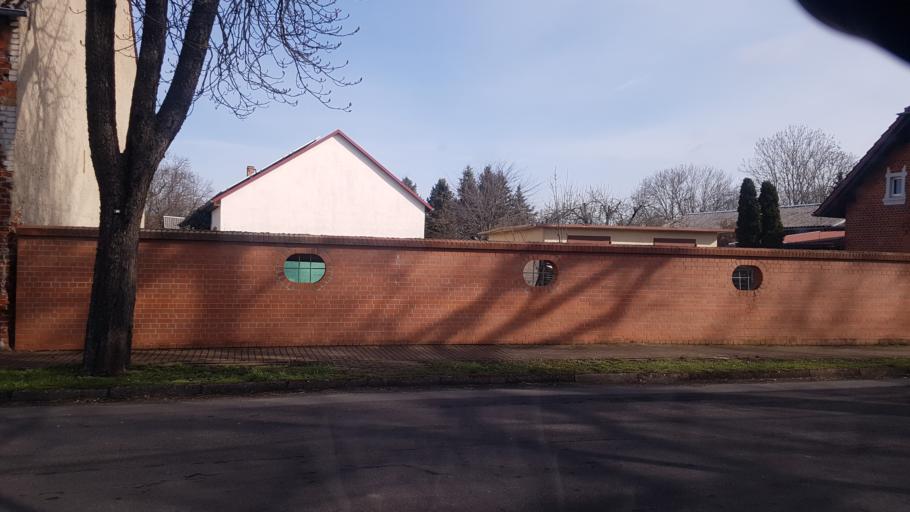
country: DE
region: Brandenburg
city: Hohenbucko
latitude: 51.6977
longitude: 13.4708
